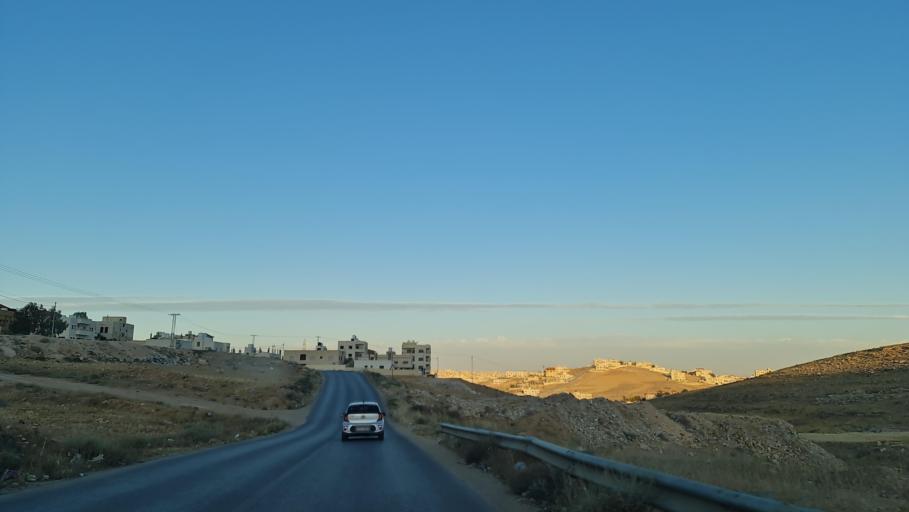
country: JO
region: Zarqa
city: Zarqa
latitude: 32.0831
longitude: 36.0500
